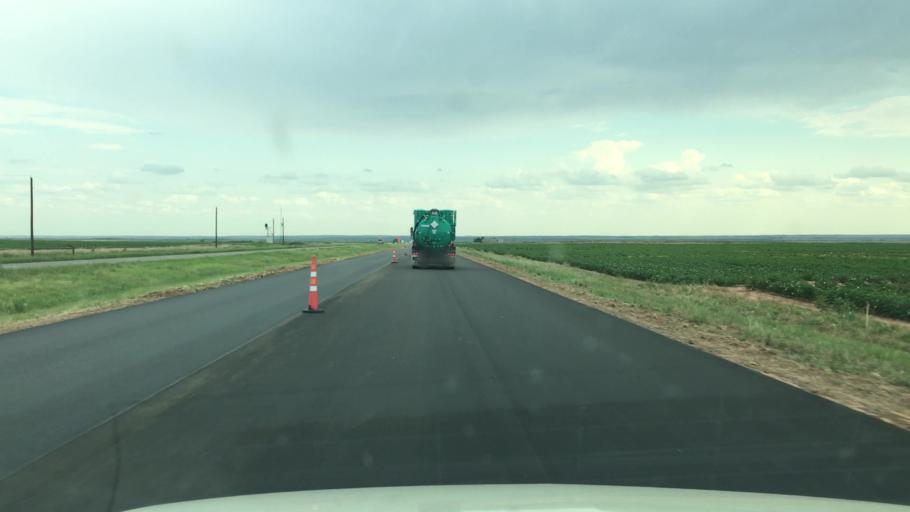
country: US
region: Texas
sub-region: Hall County
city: Memphis
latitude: 34.6281
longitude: -100.4751
